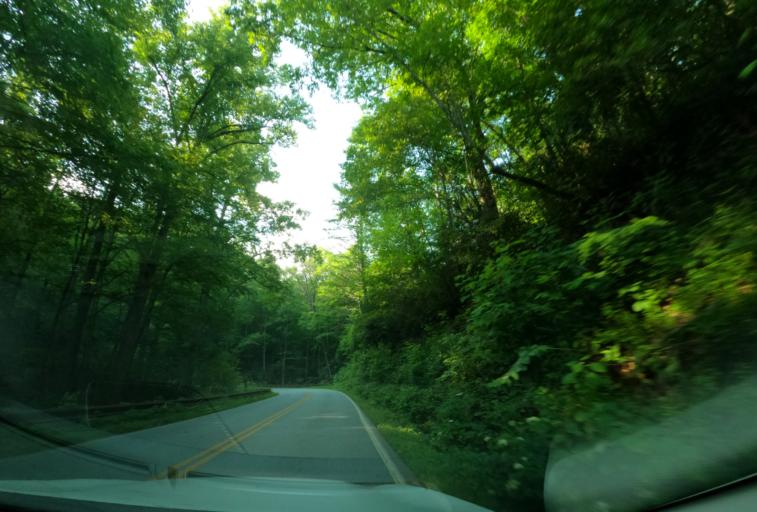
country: US
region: North Carolina
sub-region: Transylvania County
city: Brevard
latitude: 35.1963
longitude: -82.8503
